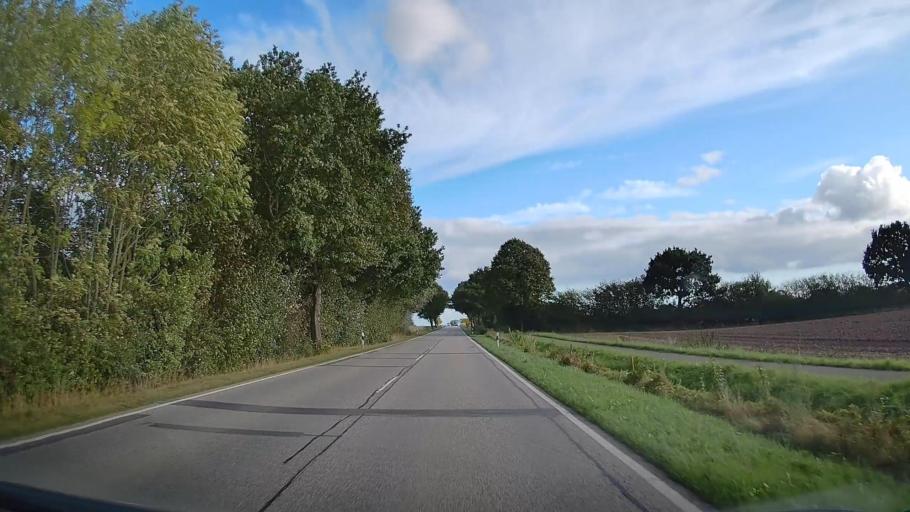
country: DE
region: Schleswig-Holstein
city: Rabel
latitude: 54.7275
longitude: 9.9475
